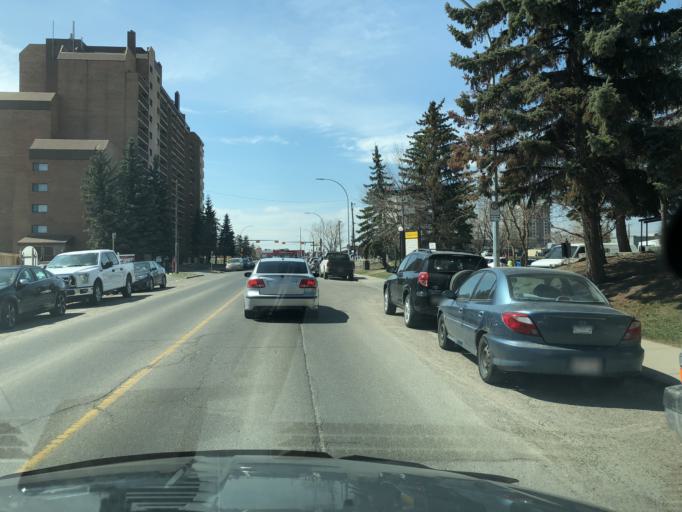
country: CA
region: Alberta
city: Calgary
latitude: 50.9723
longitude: -114.0663
